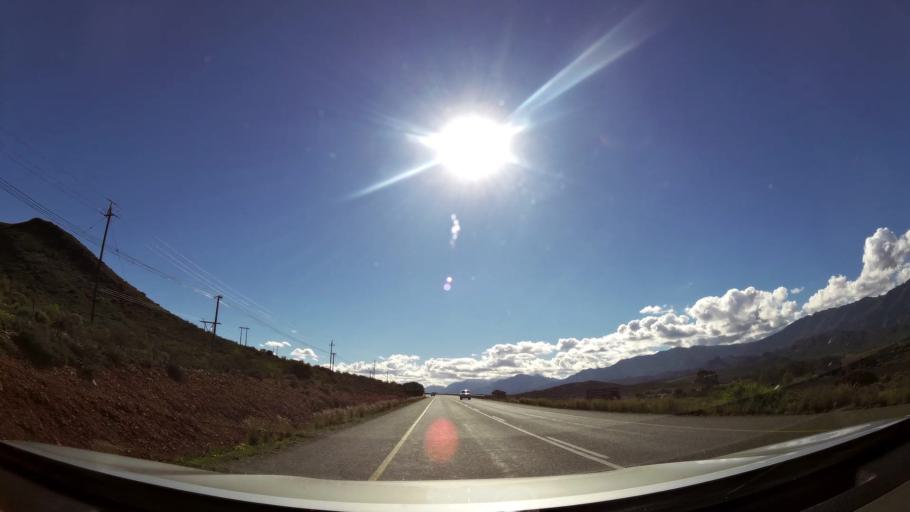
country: ZA
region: Western Cape
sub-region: Cape Winelands District Municipality
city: Ashton
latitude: -33.7808
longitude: 19.7667
